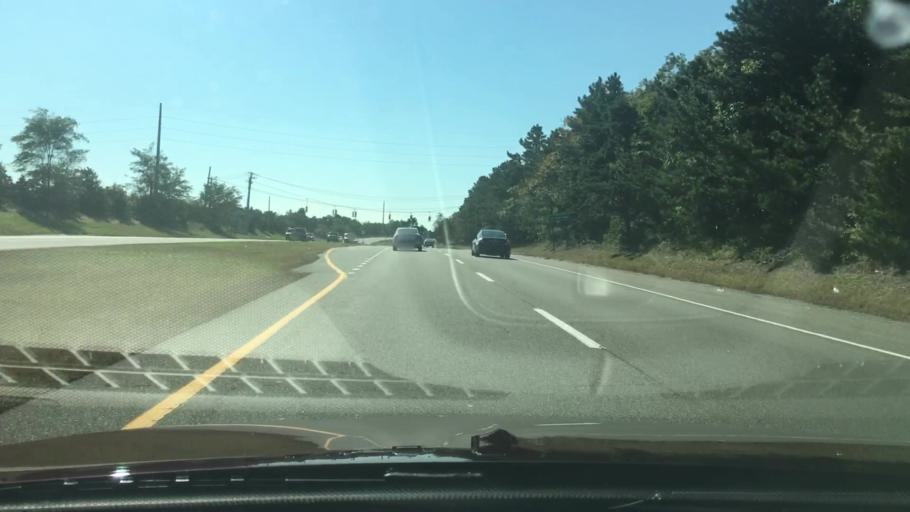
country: US
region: New York
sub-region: Suffolk County
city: Yaphank
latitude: 40.8266
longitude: -72.9399
